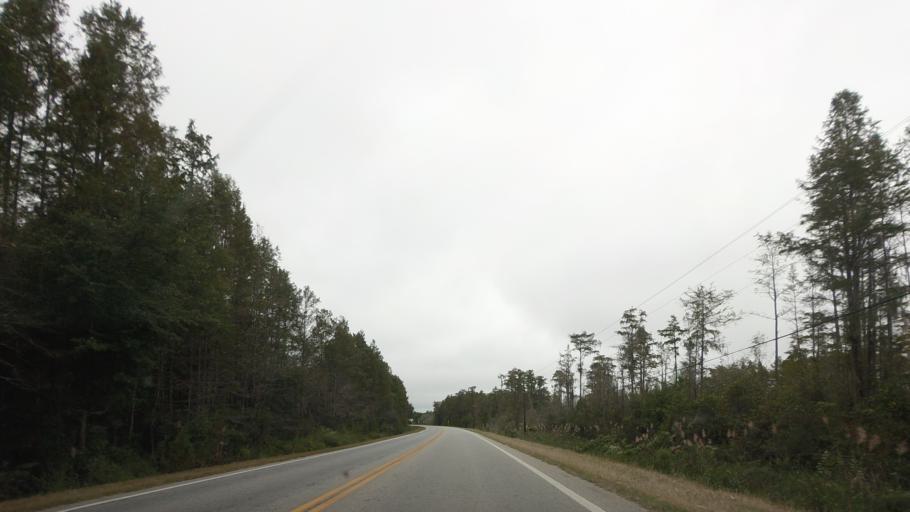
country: US
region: Georgia
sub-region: Berrien County
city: Nashville
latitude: 31.1759
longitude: -83.2340
